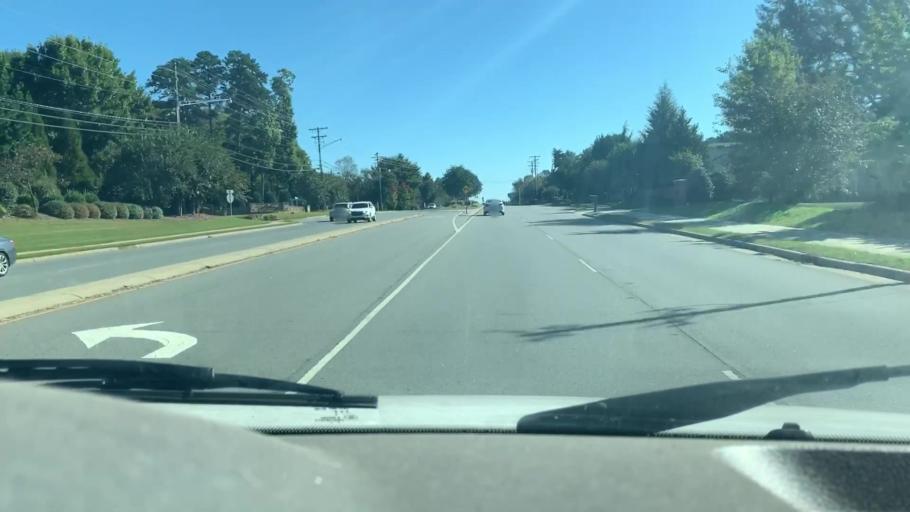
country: US
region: North Carolina
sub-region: Mecklenburg County
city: Huntersville
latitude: 35.4415
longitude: -80.8553
